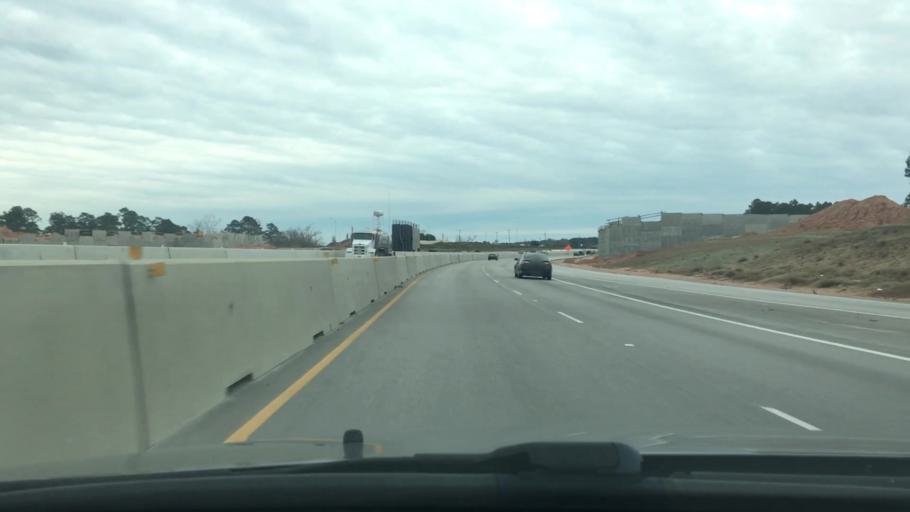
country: US
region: Texas
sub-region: Walker County
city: Huntsville
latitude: 30.6775
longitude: -95.5222
